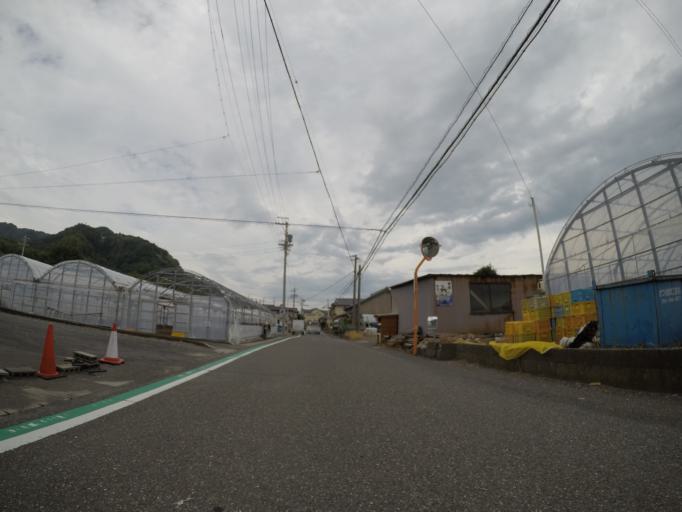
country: JP
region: Shizuoka
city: Shizuoka-shi
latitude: 34.9588
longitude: 138.4631
